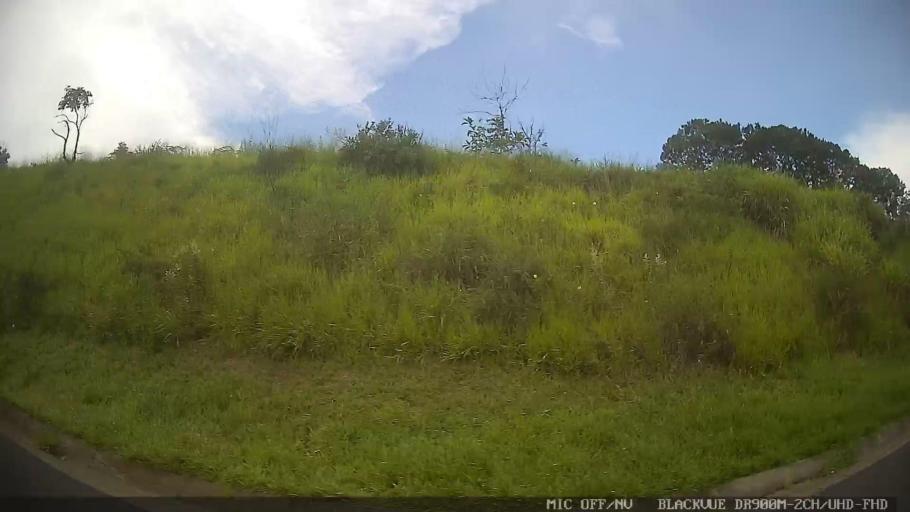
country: BR
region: Sao Paulo
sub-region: Jarinu
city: Jarinu
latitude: -23.0641
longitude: -46.6472
